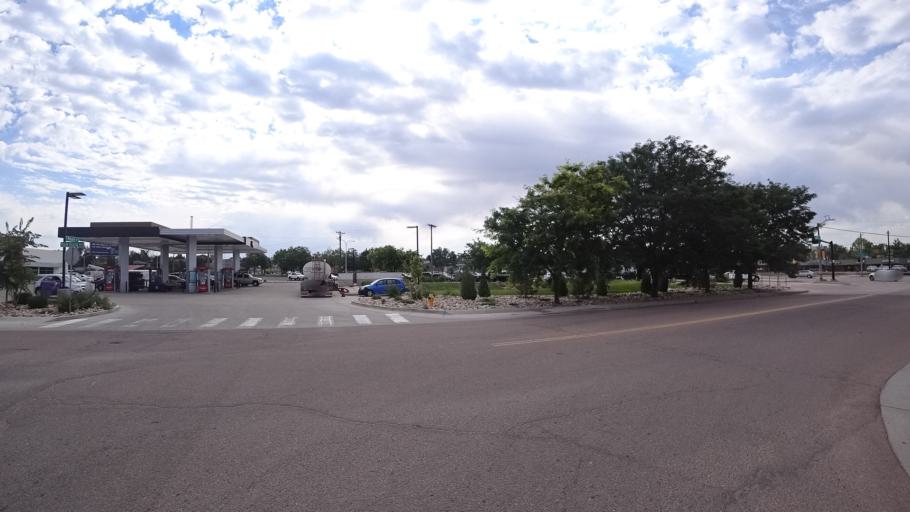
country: US
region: Colorado
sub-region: El Paso County
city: Cimarron Hills
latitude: 38.8977
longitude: -104.7481
